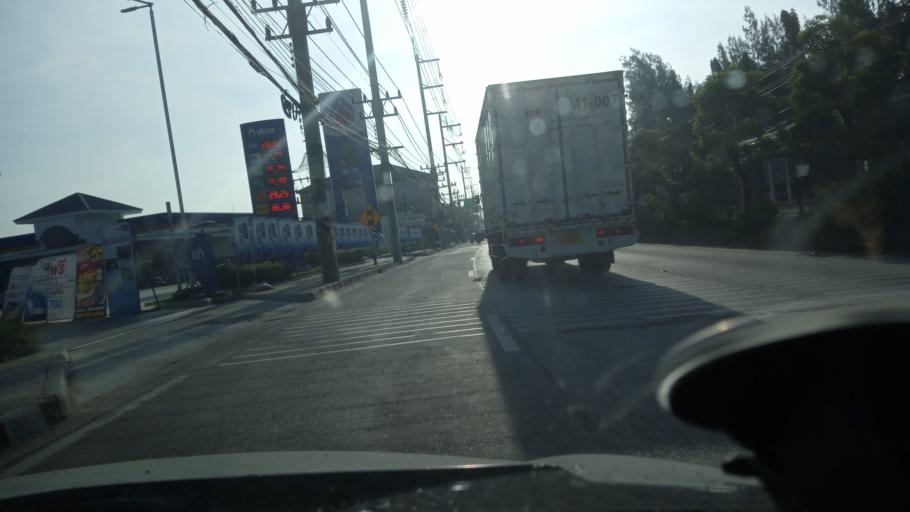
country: TH
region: Chon Buri
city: Phan Thong
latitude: 13.4146
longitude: 101.0625
